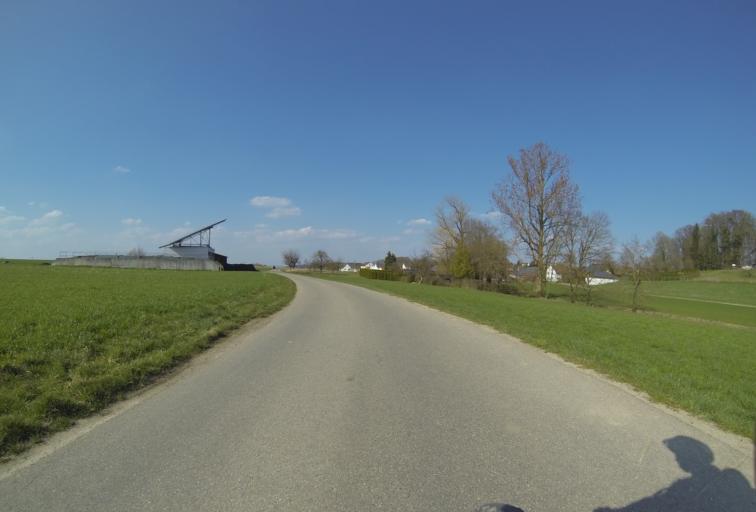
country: DE
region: Baden-Wuerttemberg
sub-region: Tuebingen Region
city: Huttisheim
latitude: 48.2572
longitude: 9.9525
